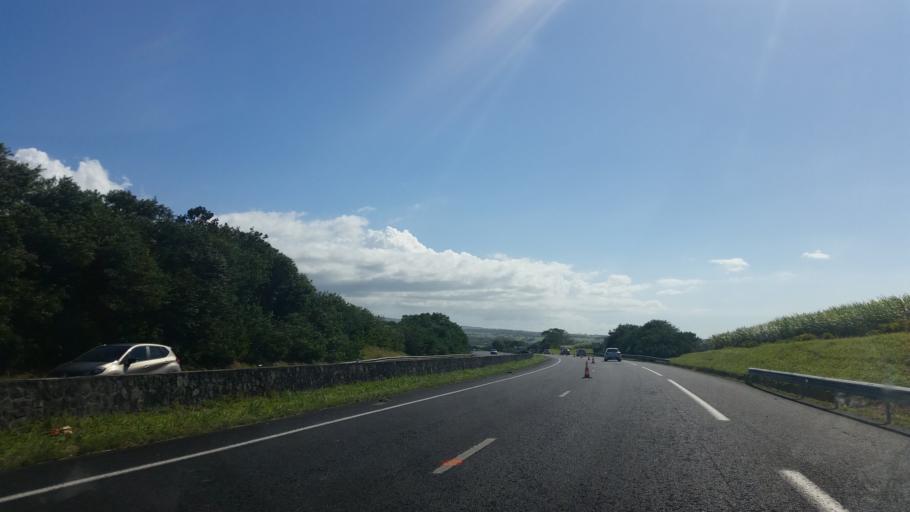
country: RE
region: Reunion
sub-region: Reunion
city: Bras-Panon
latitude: -21.0177
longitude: 55.6970
